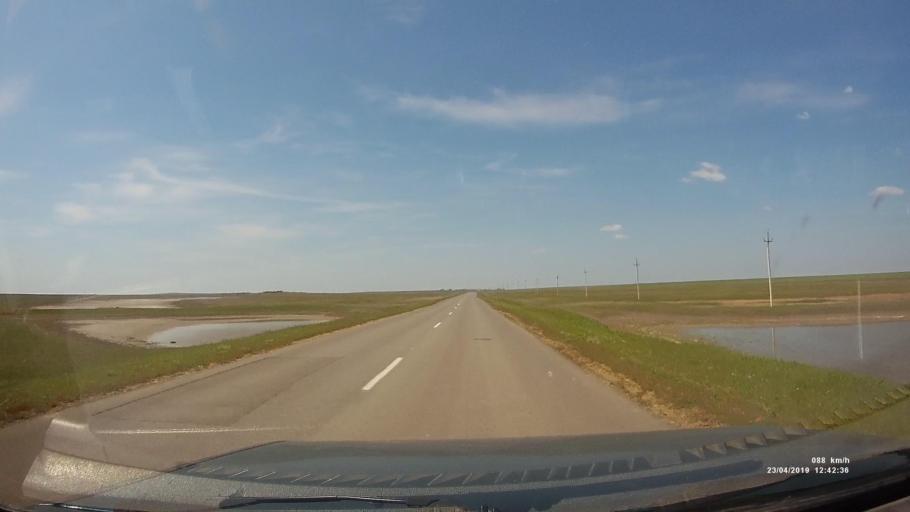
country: RU
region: Kalmykiya
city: Yashalta
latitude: 46.4571
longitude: 42.6633
